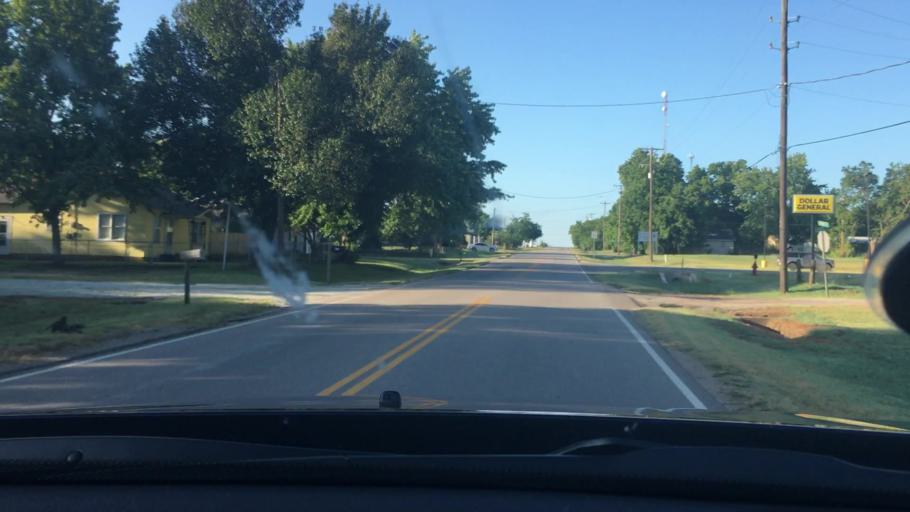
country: US
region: Oklahoma
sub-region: Murray County
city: Sulphur
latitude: 34.6245
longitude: -96.8447
